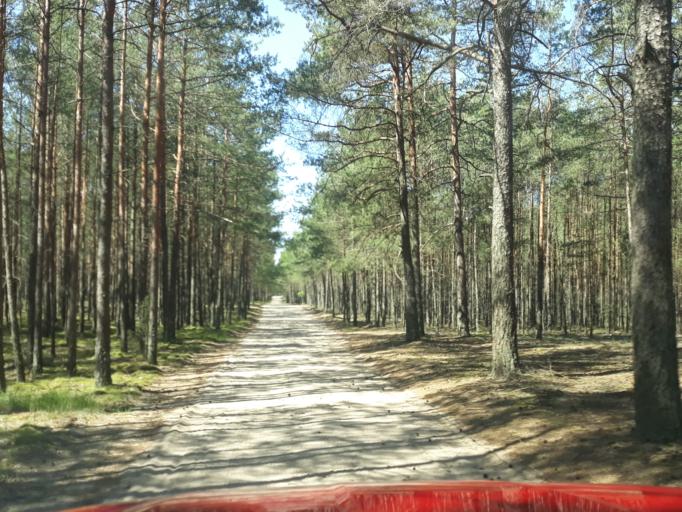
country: PL
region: Pomeranian Voivodeship
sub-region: Powiat chojnicki
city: Chojnice
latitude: 53.8672
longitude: 17.5396
